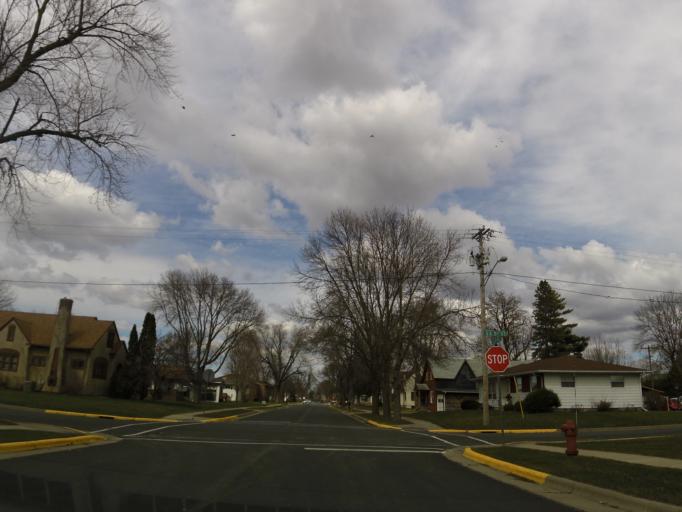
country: US
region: Minnesota
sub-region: Goodhue County
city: Pine Island
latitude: 44.1980
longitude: -92.6450
